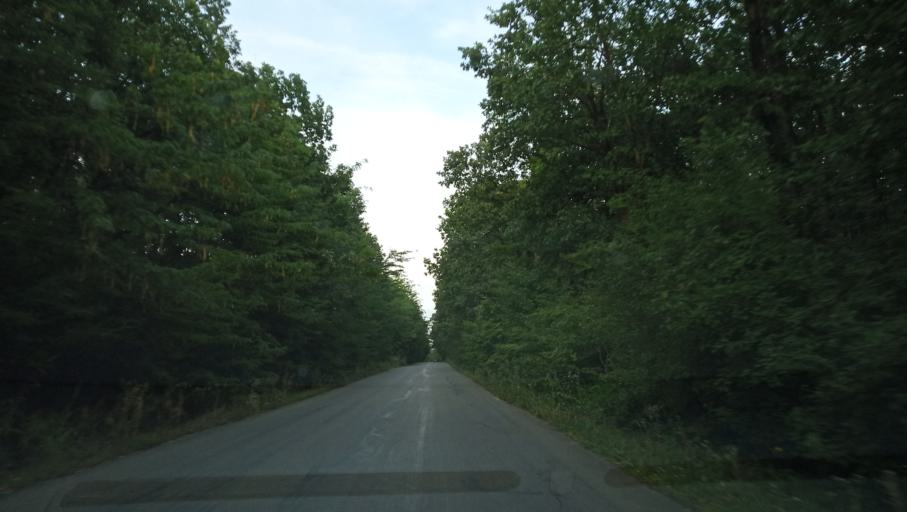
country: RO
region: Giurgiu
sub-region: Comuna Comana
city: Comana
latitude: 44.1697
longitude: 26.1624
